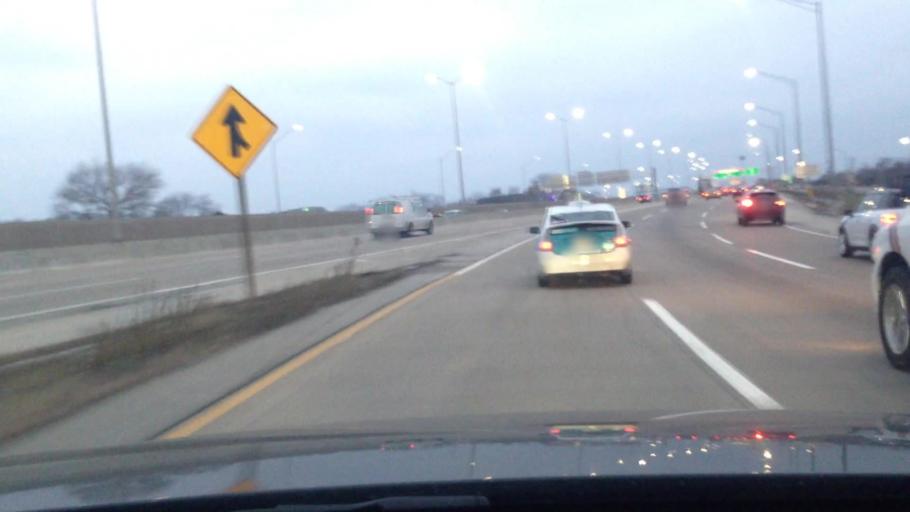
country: US
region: Illinois
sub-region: Cook County
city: Rosemont
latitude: 41.9933
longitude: -87.8716
